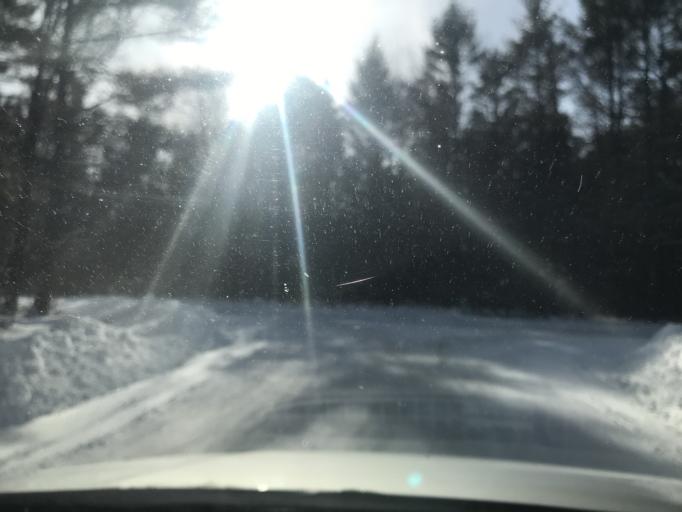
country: US
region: Wisconsin
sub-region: Oconto County
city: Gillett
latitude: 45.1369
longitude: -88.2502
